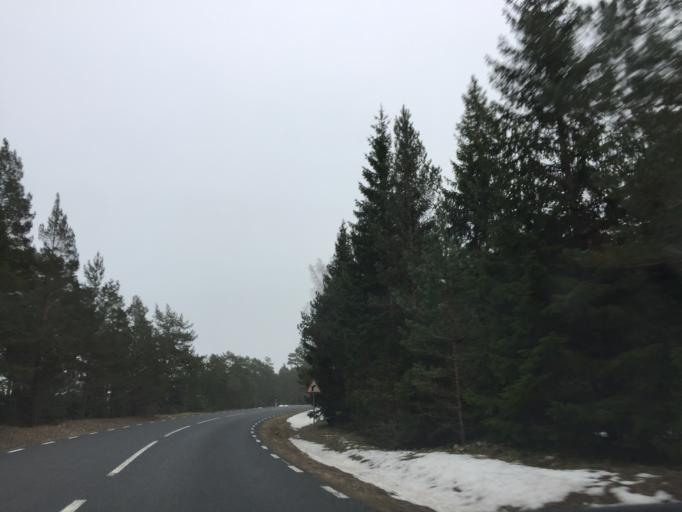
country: EE
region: Saare
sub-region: Kuressaare linn
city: Kuressaare
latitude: 58.4647
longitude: 22.0449
